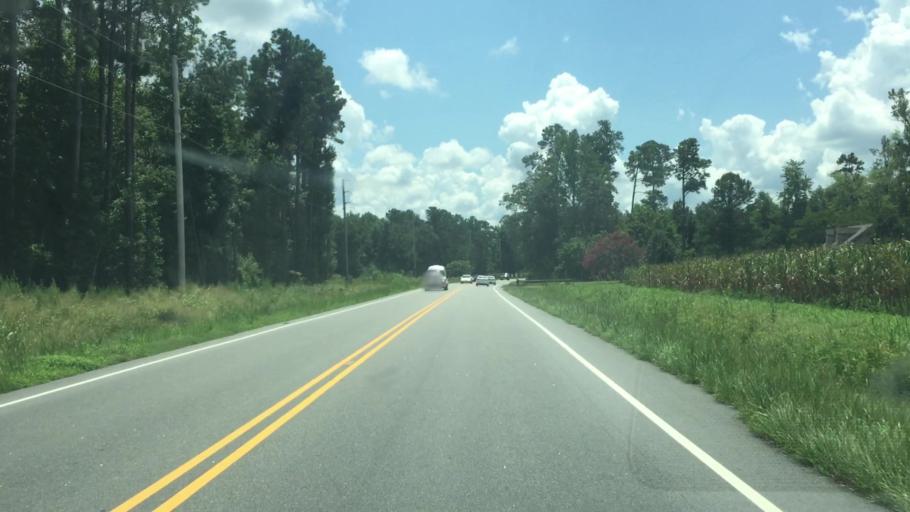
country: US
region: North Carolina
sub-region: Columbus County
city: Tabor City
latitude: 34.2184
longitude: -78.8240
